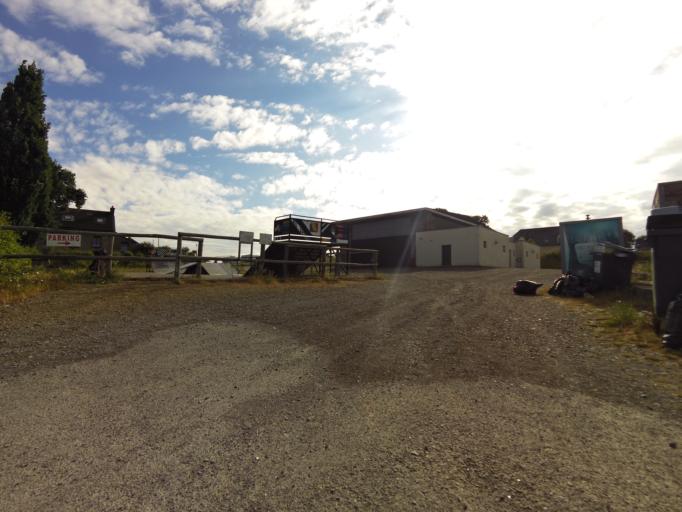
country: FR
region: Brittany
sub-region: Departement d'Ille-et-Vilaine
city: Saint-Medard-sur-Ille
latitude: 48.2520
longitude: -1.6574
